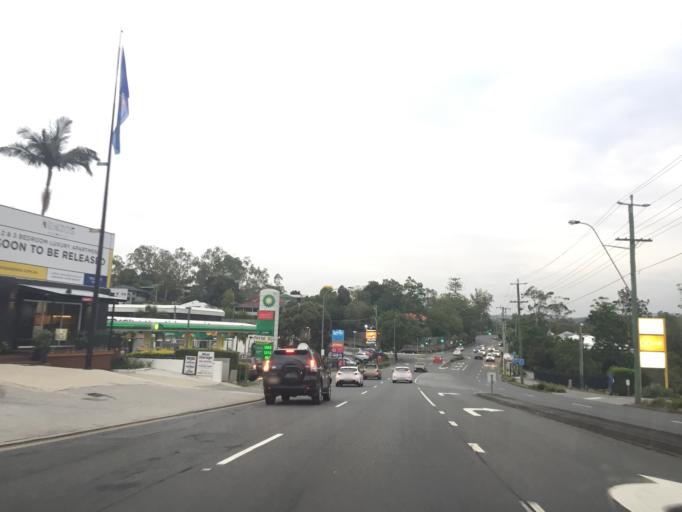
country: AU
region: Queensland
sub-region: Brisbane
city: Toowong
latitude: -27.4465
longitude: 152.9603
